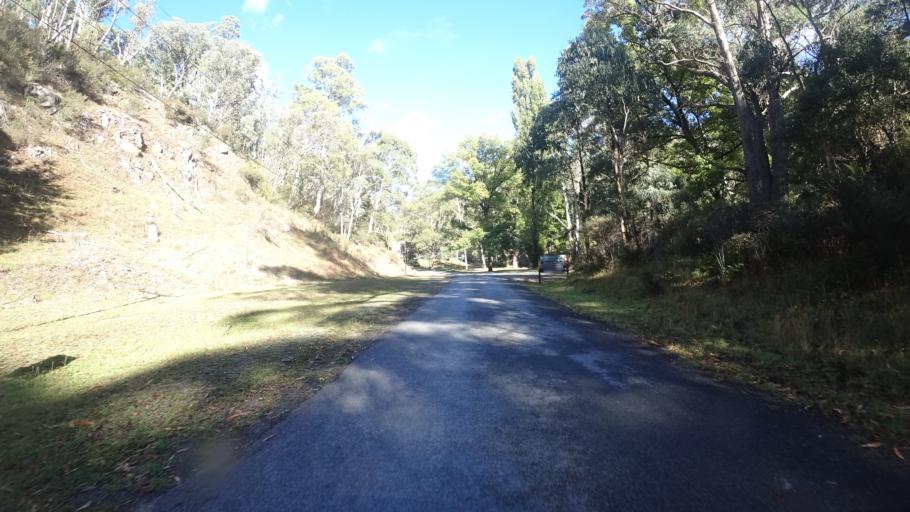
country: AU
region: New South Wales
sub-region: Tumut Shire
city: Tumut
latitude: -35.7246
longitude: 148.4940
